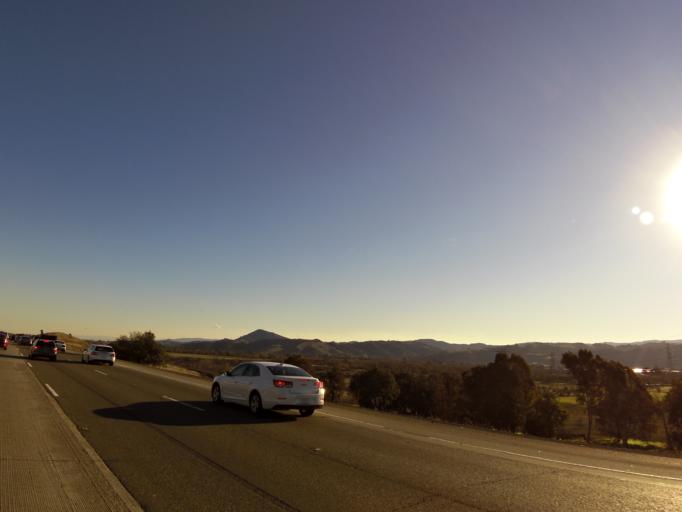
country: US
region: California
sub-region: Santa Clara County
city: Morgan Hill
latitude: 37.1838
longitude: -121.6847
